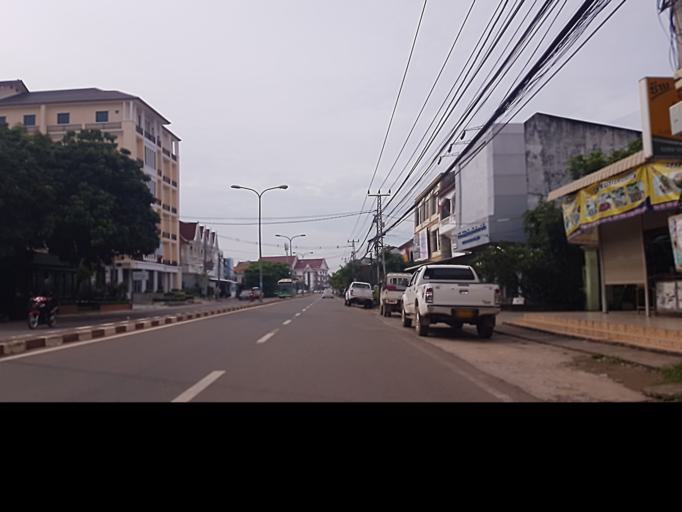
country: LA
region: Vientiane
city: Vientiane
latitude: 17.9491
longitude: 102.6195
